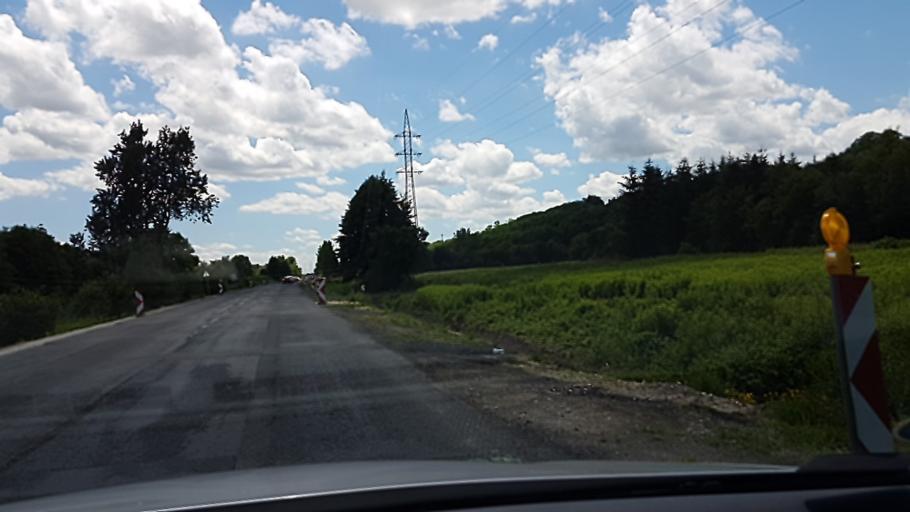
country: HU
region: Zala
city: Zalaegerszeg
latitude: 46.8279
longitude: 16.8635
